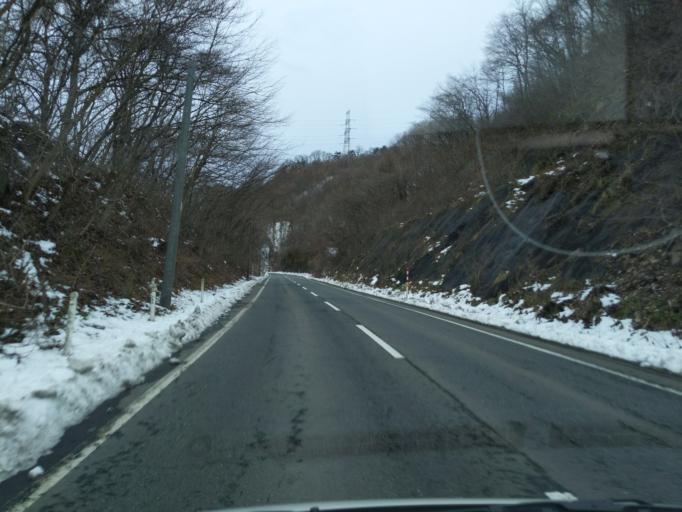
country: JP
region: Iwate
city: Mizusawa
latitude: 39.1005
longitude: 141.2657
